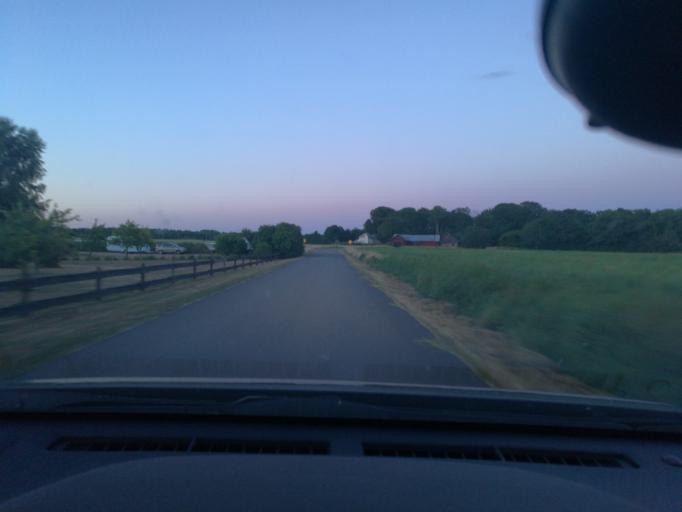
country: SE
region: Kalmar
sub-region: Borgholms Kommun
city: Borgholm
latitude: 56.8704
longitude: 16.7259
